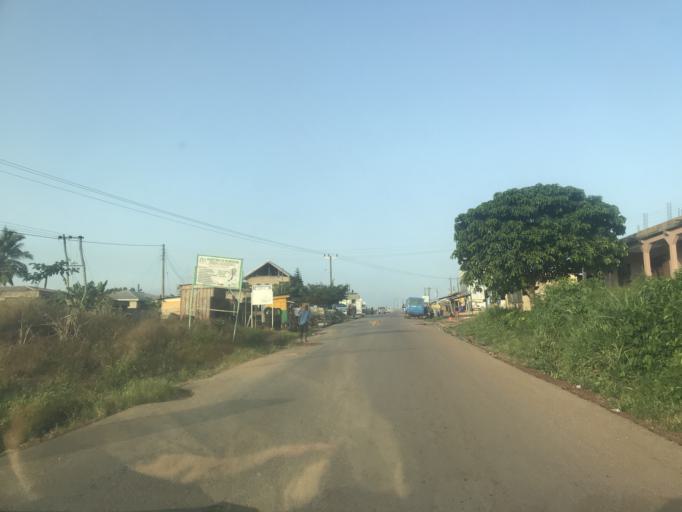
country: GH
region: Ashanti
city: Obuasi
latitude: 6.2034
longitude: -1.6060
